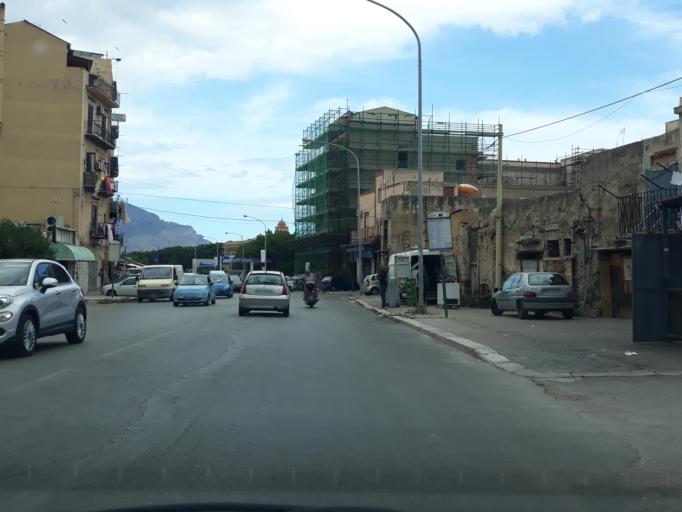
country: IT
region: Sicily
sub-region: Palermo
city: Ciaculli
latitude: 38.1112
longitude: 13.3785
